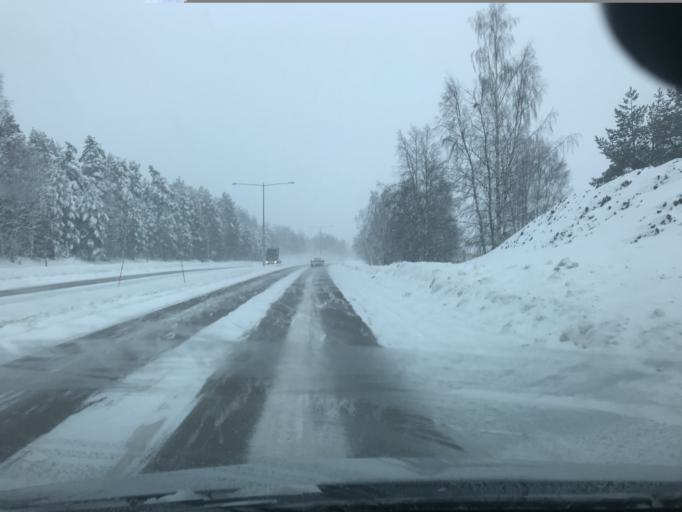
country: SE
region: Norrbotten
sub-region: Lulea Kommun
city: Lulea
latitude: 65.6090
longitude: 22.1369
